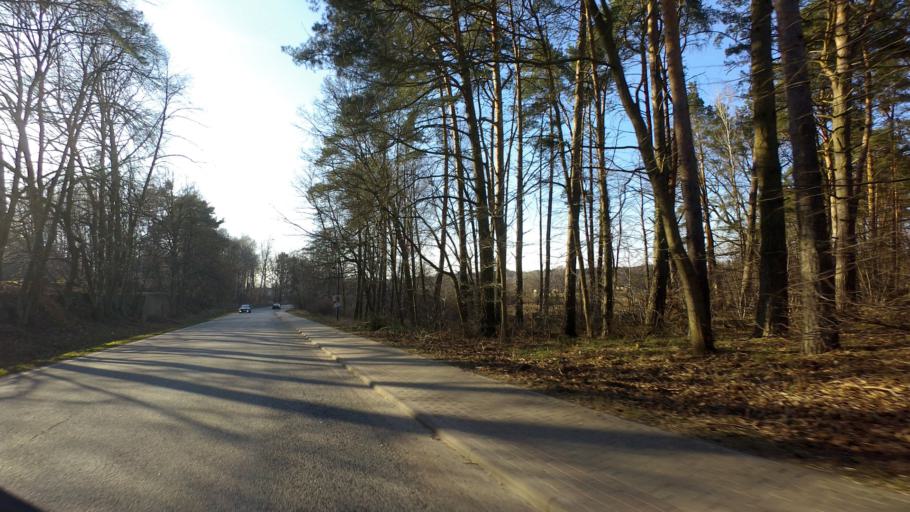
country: DE
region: Brandenburg
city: Althuttendorf
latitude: 52.9556
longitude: 13.7961
